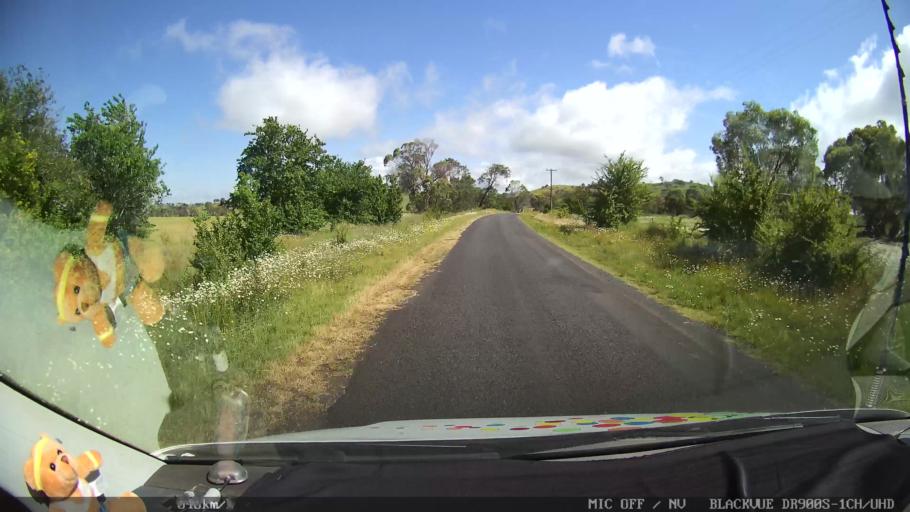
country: AU
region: New South Wales
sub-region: Guyra
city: Guyra
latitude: -30.0156
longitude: 151.6574
